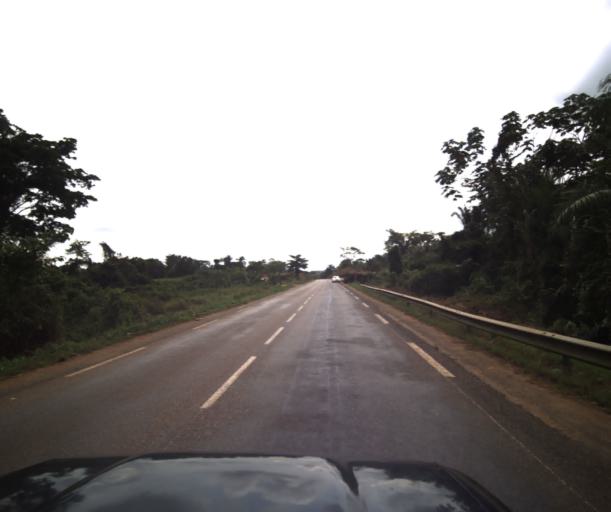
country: CM
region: Centre
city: Eseka
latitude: 3.8489
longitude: 10.5001
